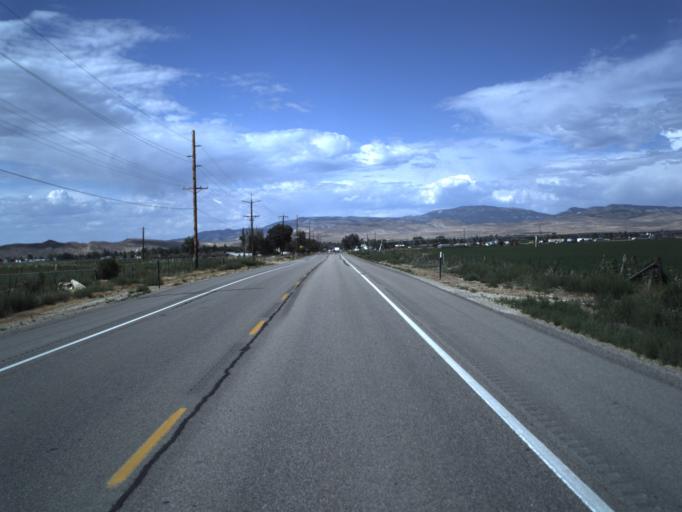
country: US
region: Utah
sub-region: Sanpete County
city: Centerfield
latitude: 39.1063
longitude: -111.8197
